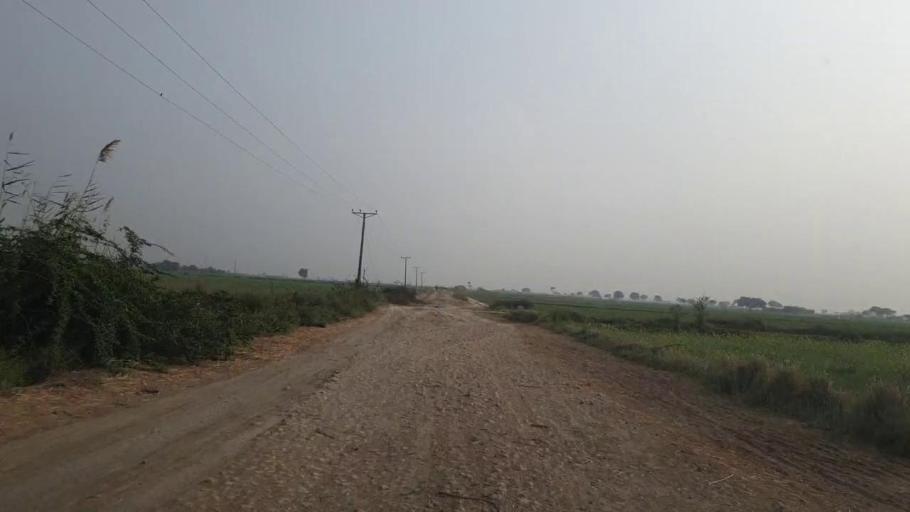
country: PK
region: Sindh
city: Mirpur Batoro
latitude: 24.5622
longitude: 68.4186
